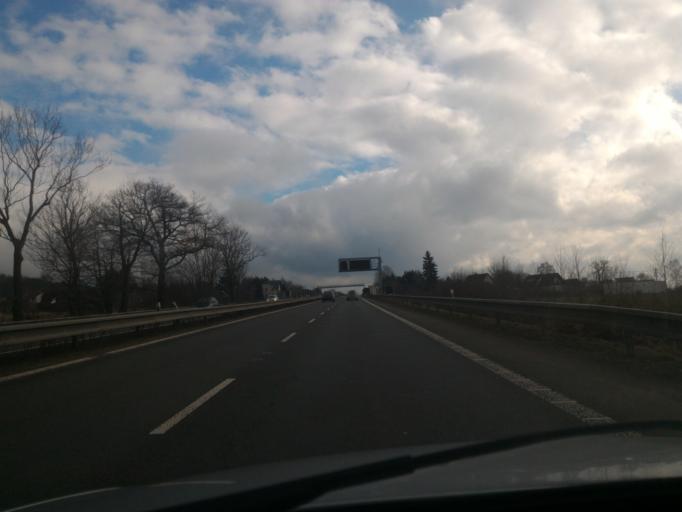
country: CZ
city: Chrastava
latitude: 50.7995
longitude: 14.9904
